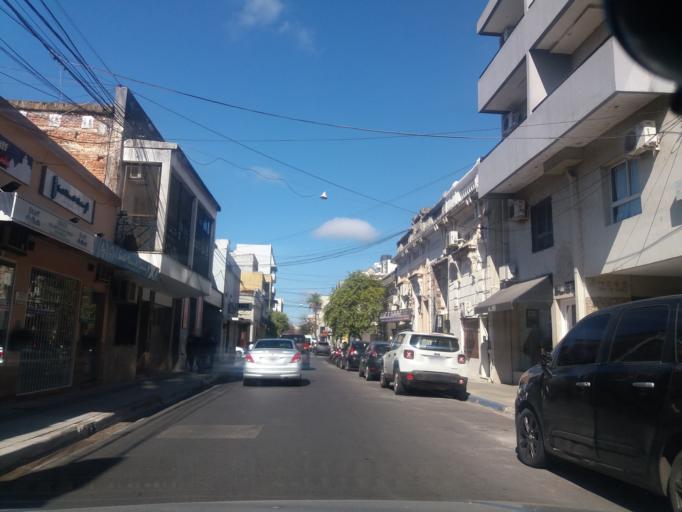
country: AR
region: Corrientes
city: Corrientes
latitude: -27.4695
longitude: -58.8346
